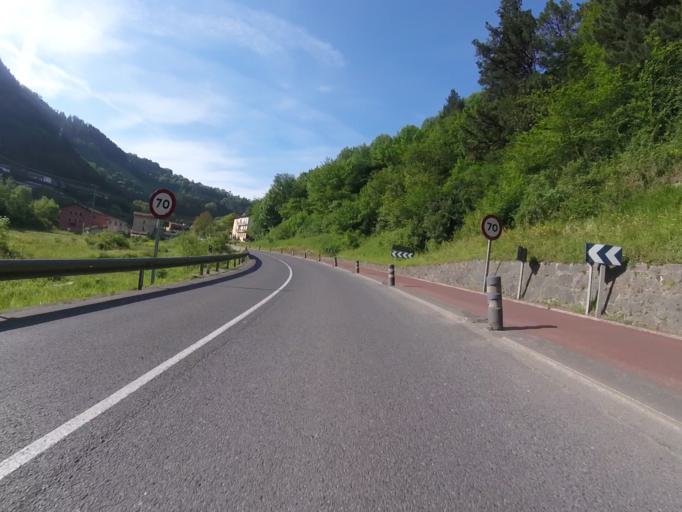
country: ES
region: Basque Country
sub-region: Provincia de Guipuzcoa
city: Isasondo
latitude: 43.0729
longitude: -2.1637
